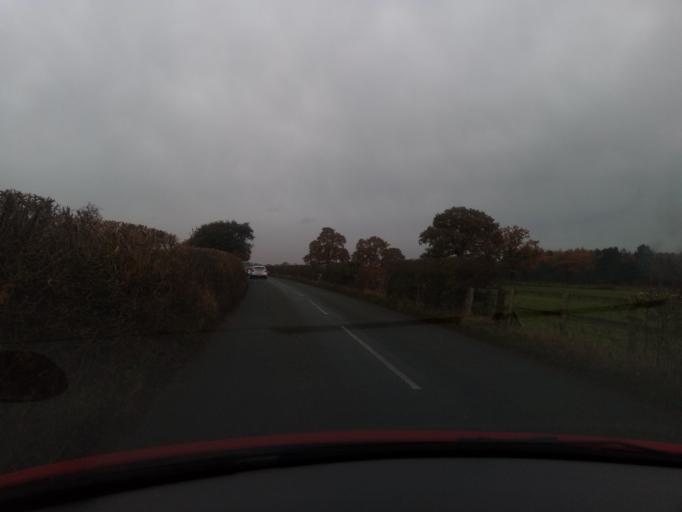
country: GB
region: England
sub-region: Derbyshire
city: Borrowash
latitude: 52.9427
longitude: -1.4059
